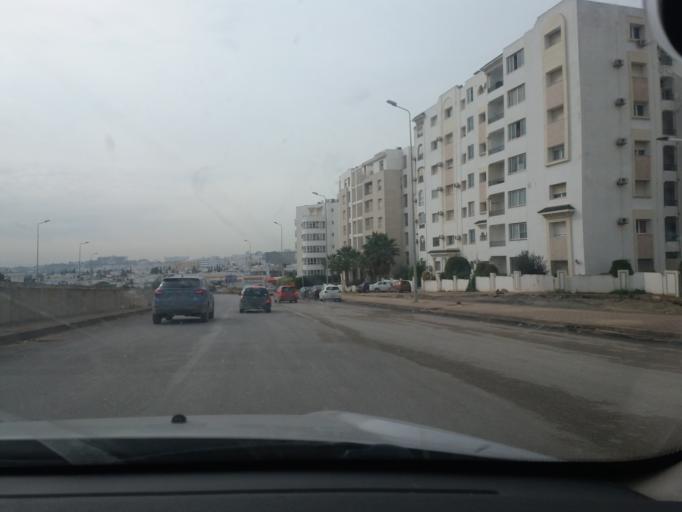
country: TN
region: Tunis
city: Tunis
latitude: 36.8544
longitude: 10.1525
